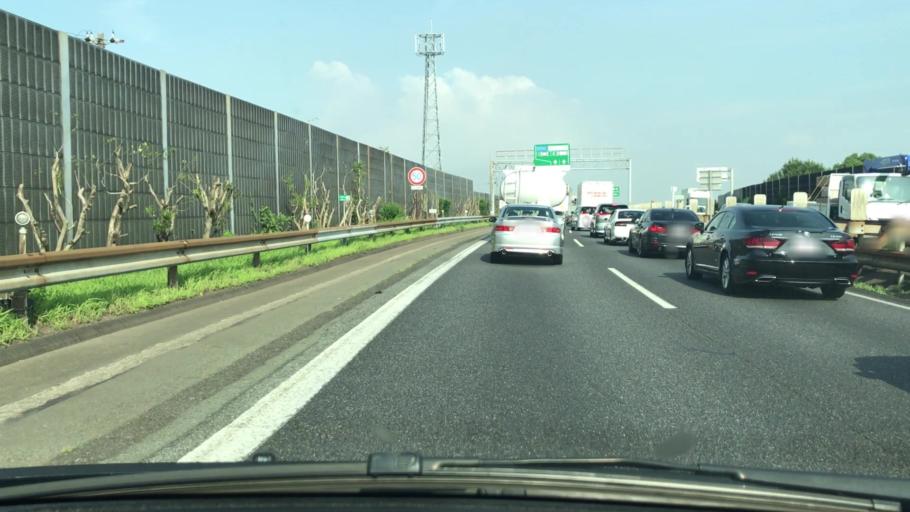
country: JP
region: Hyogo
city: Kakogawacho-honmachi
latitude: 34.7166
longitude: 134.9049
